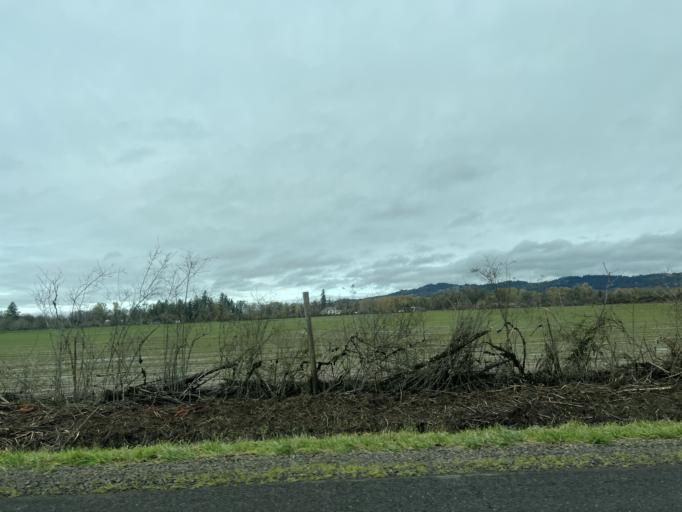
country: US
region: Oregon
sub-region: Polk County
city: Independence
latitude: 44.7908
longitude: -123.0958
